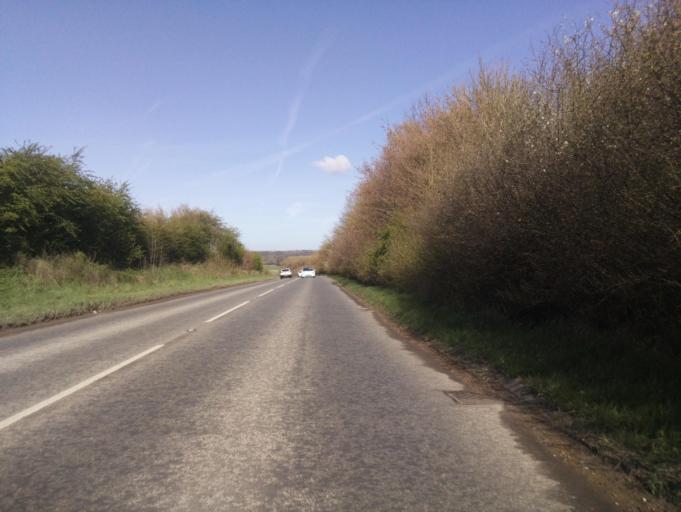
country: GB
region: England
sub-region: Wiltshire
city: Bradford-on-Avon
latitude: 51.3664
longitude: -2.2677
